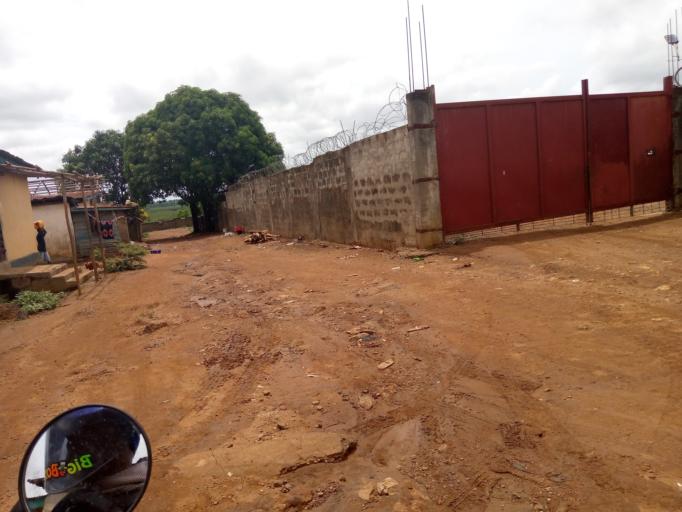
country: SL
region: Western Area
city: Hastings
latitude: 8.4132
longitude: -13.1421
